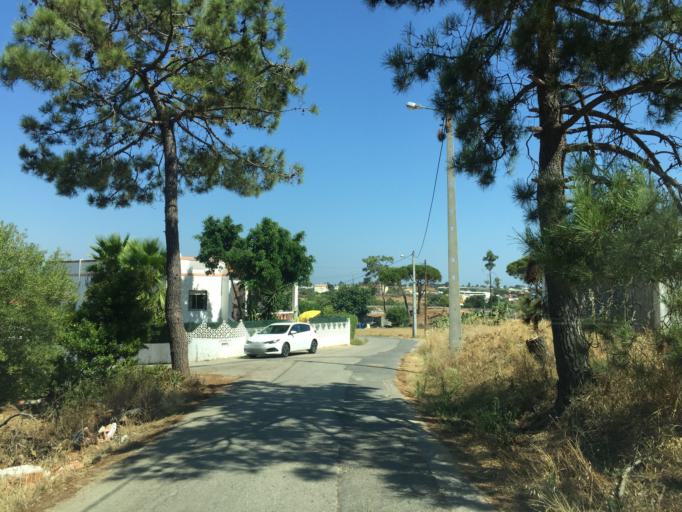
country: PT
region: Faro
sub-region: Faro
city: Faro
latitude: 37.0429
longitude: -7.8955
